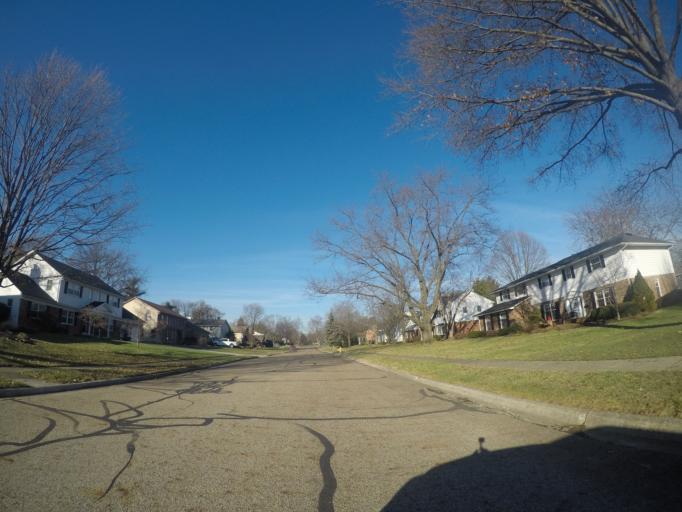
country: US
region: Ohio
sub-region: Franklin County
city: Upper Arlington
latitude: 40.0364
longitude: -83.0703
